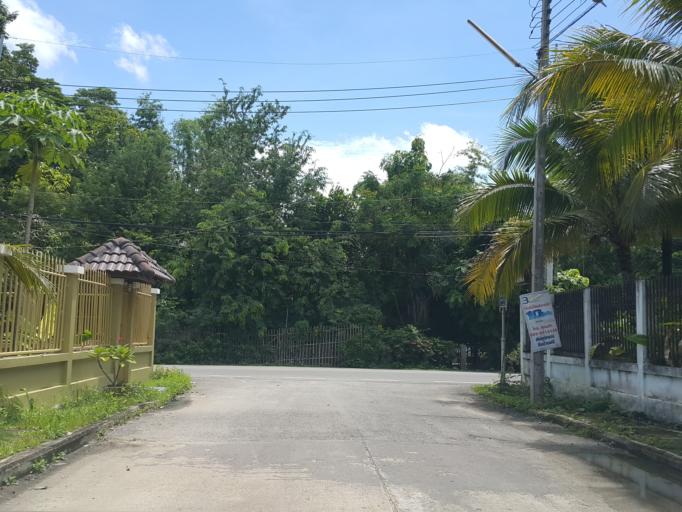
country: TH
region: Chiang Mai
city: San Kamphaeng
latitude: 18.7602
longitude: 99.1001
